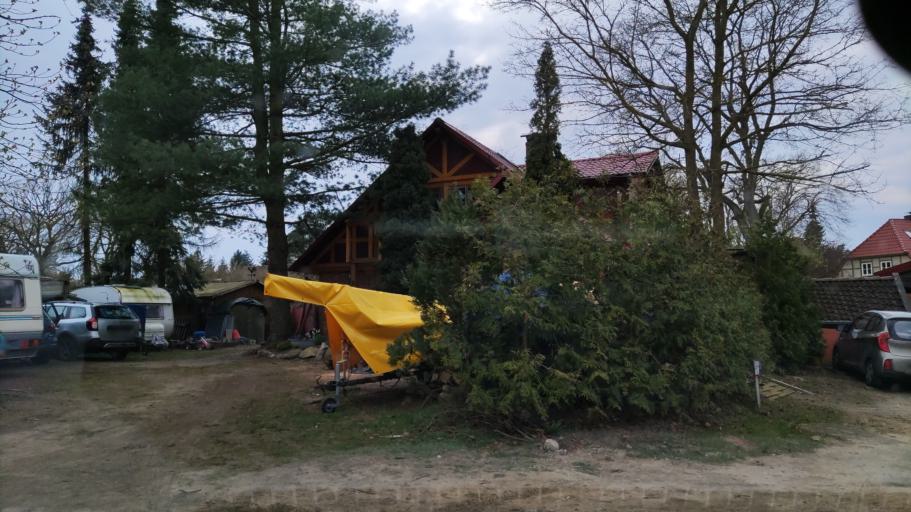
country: DE
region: Lower Saxony
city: Tosterglope
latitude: 53.2765
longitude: 10.8054
